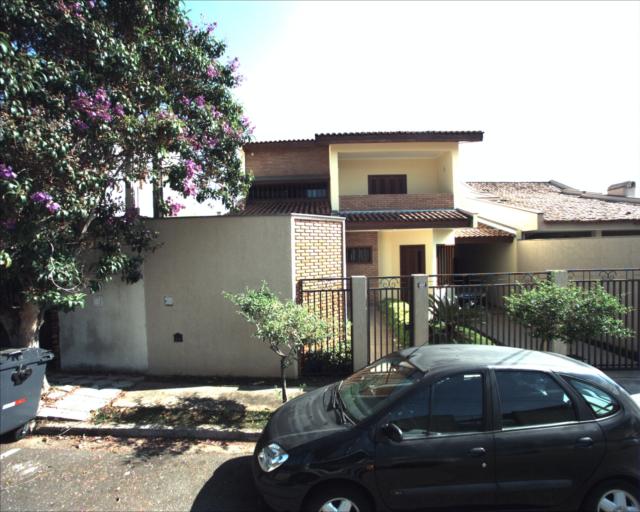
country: BR
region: Sao Paulo
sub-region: Sorocaba
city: Sorocaba
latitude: -23.4829
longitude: -47.4422
